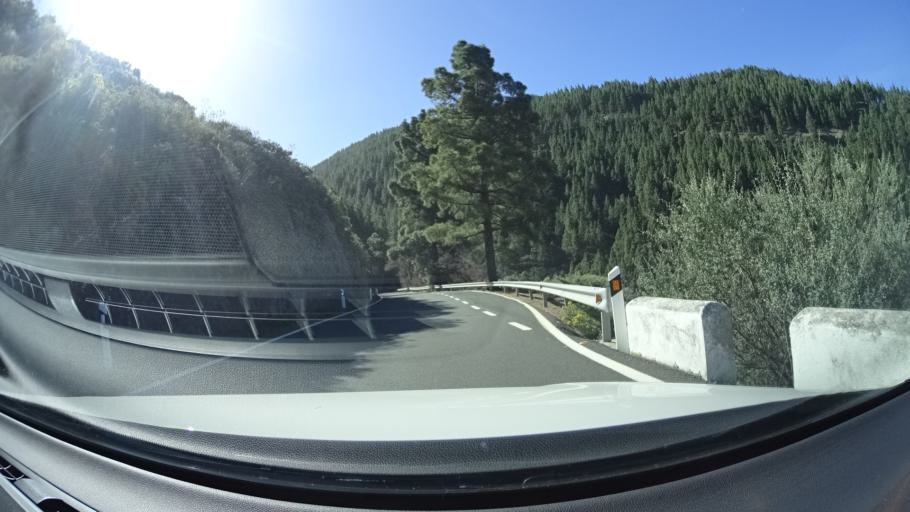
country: ES
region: Canary Islands
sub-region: Provincia de Las Palmas
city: Artenara
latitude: 28.0244
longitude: -15.6235
